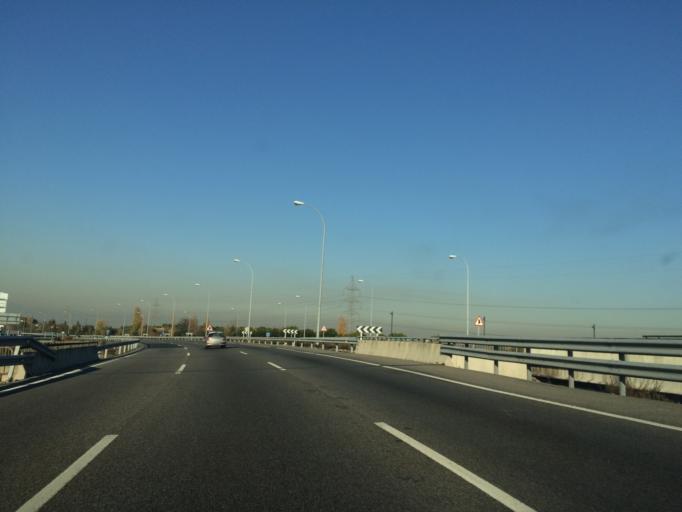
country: ES
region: Madrid
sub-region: Provincia de Madrid
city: Pozuelo de Alarcon
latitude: 40.4108
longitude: -3.8217
